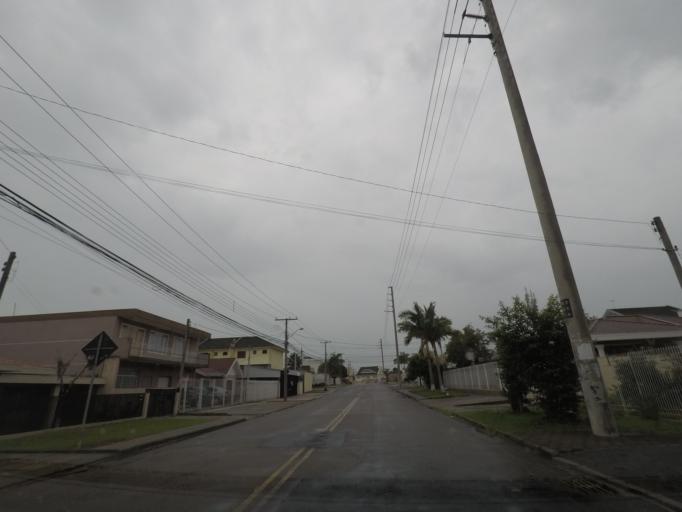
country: BR
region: Parana
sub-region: Curitiba
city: Curitiba
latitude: -25.4744
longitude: -49.3106
